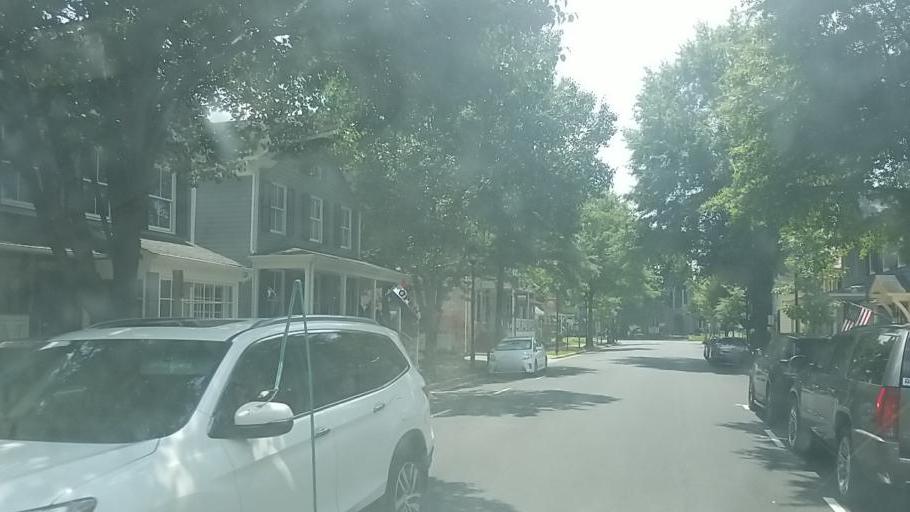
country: US
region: Maryland
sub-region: Talbot County
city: Easton
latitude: 38.7735
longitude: -76.0747
